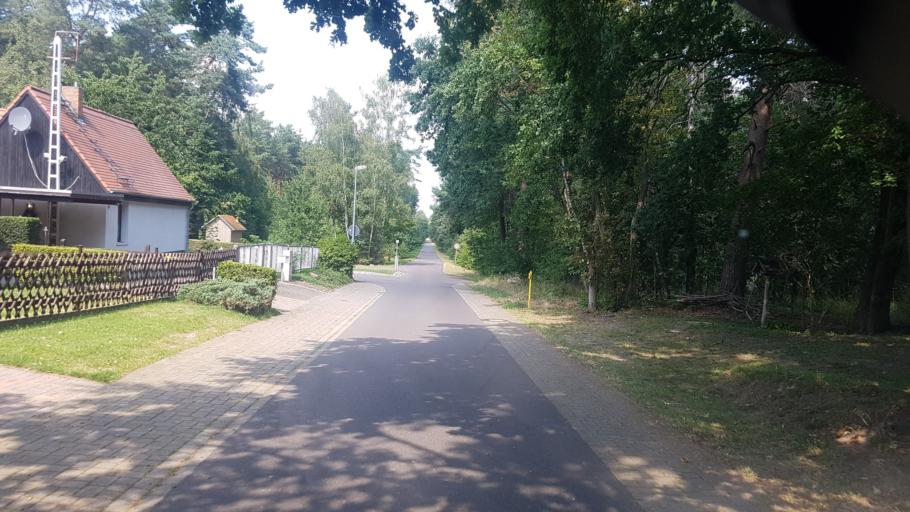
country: DE
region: Brandenburg
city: Spremberg
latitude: 51.6115
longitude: 14.3998
